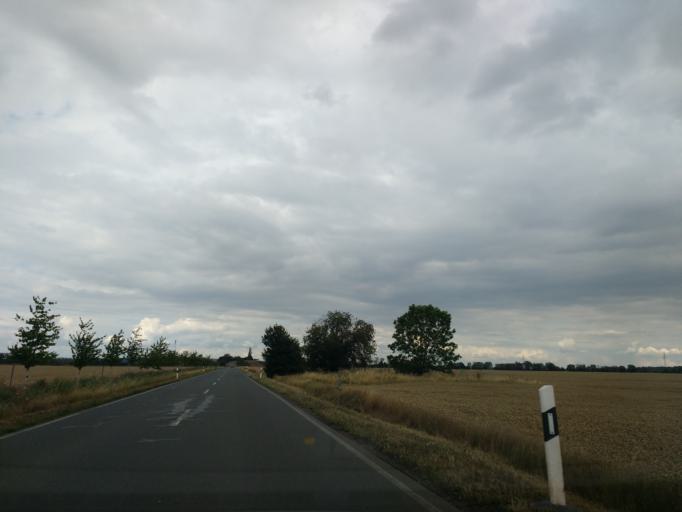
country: DE
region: Saxony-Anhalt
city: Dolbau
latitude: 51.4632
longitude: 12.0812
